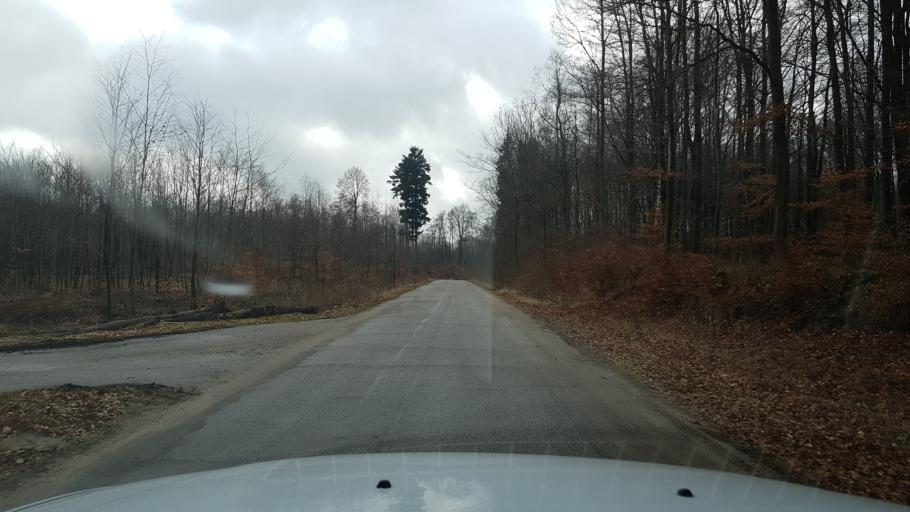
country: PL
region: West Pomeranian Voivodeship
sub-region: Powiat szczecinecki
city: Szczecinek
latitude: 53.6993
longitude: 16.7664
